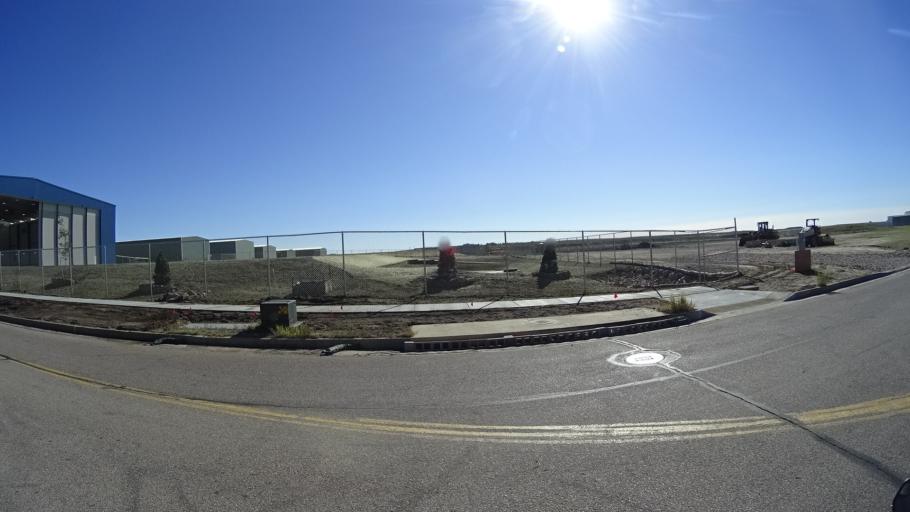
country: US
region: Colorado
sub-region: El Paso County
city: Security-Widefield
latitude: 38.7991
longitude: -104.7237
